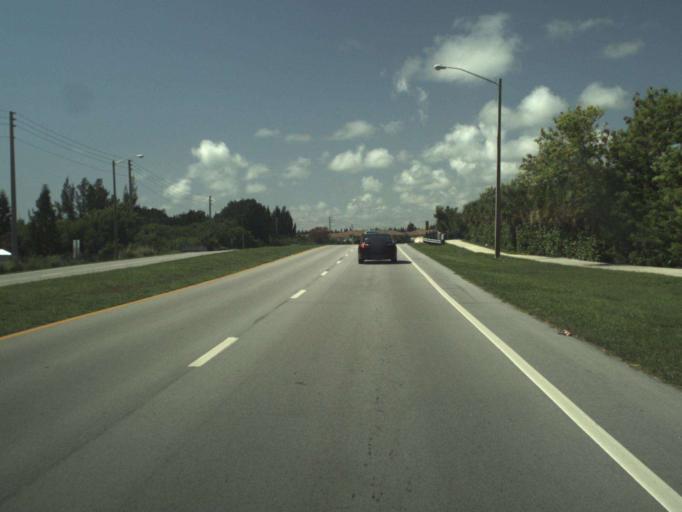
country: US
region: Florida
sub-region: Indian River County
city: Vero Beach
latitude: 27.6281
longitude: -80.3787
